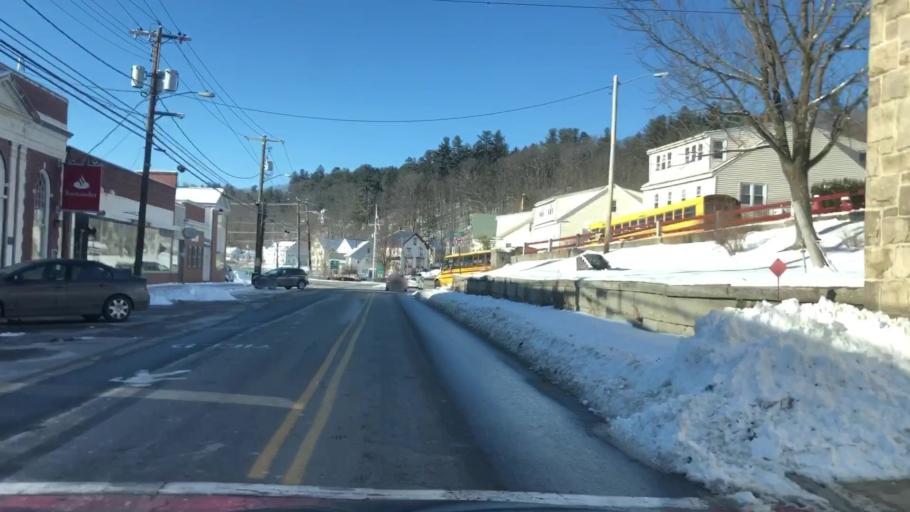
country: US
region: New Hampshire
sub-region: Hillsborough County
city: Wilton
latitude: 42.8438
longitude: -71.7378
